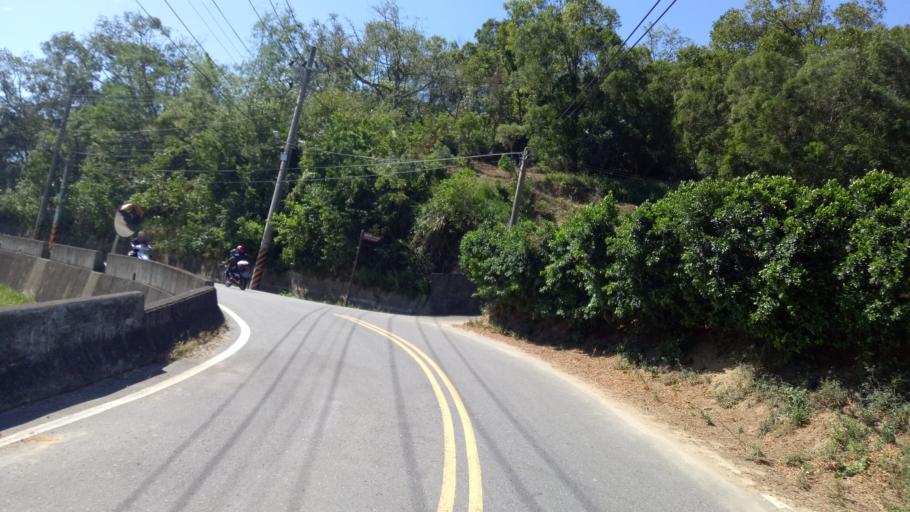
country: TW
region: Taiwan
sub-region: Hsinchu
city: Hsinchu
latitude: 24.7414
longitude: 120.9563
